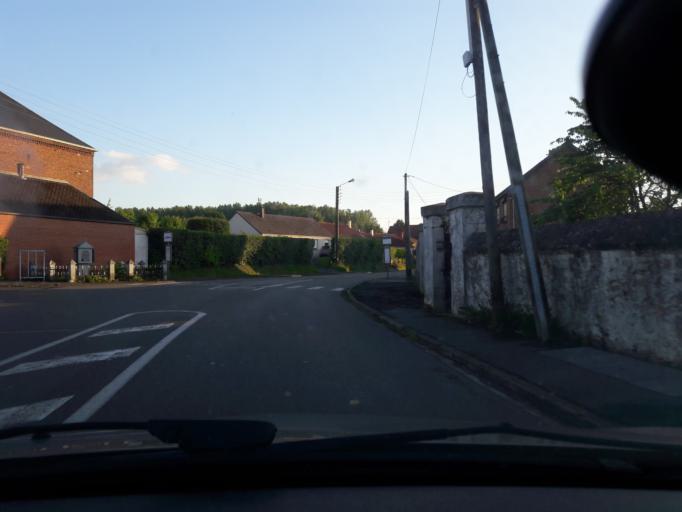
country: FR
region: Nord-Pas-de-Calais
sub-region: Departement du Nord
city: Marpent
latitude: 50.2898
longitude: 4.0771
